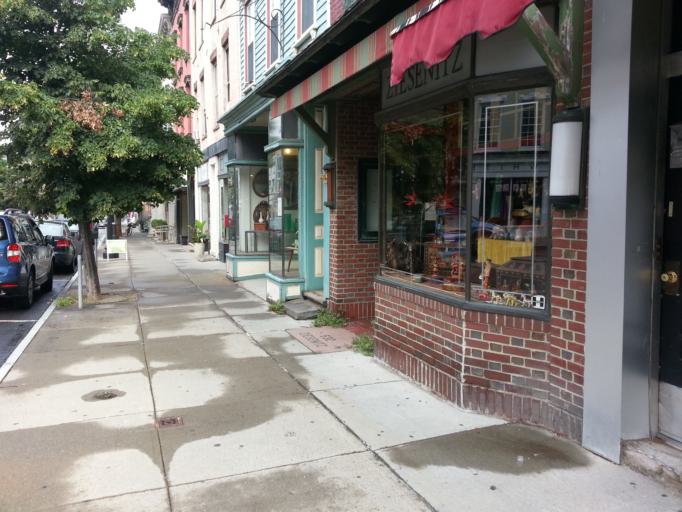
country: US
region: New York
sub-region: Columbia County
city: Oakdale
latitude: 42.2488
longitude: -73.7855
